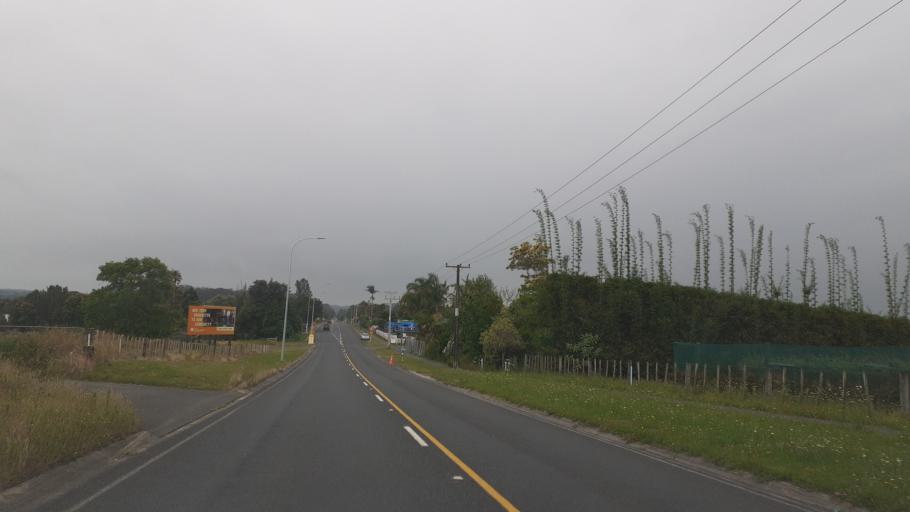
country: NZ
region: Northland
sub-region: Far North District
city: Kerikeri
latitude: -35.2368
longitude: 173.9407
